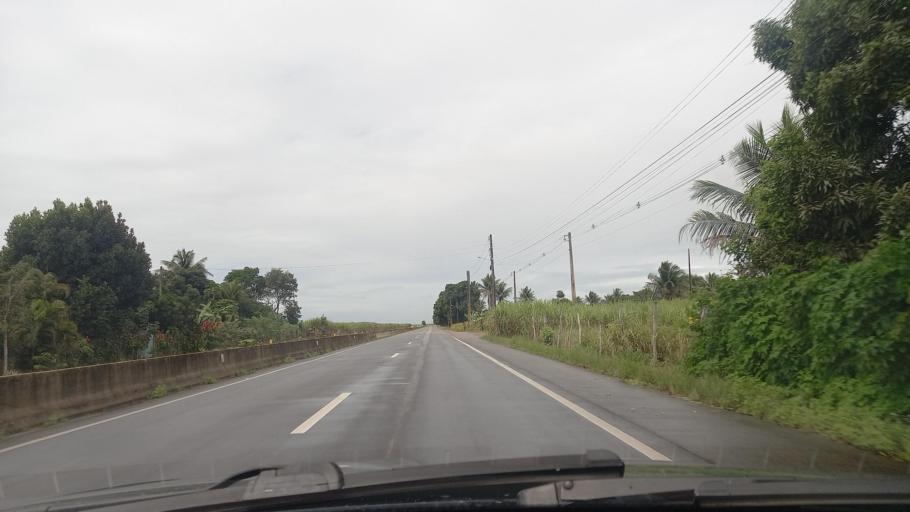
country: BR
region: Alagoas
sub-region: Campo Alegre
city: Campo Alegre
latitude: -9.8165
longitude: -36.2503
